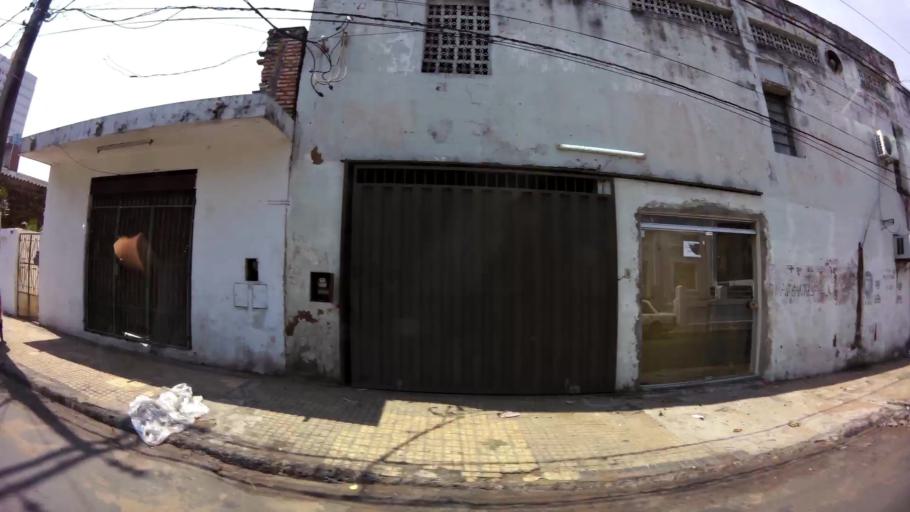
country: PY
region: Asuncion
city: Asuncion
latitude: -25.2907
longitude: -57.6481
